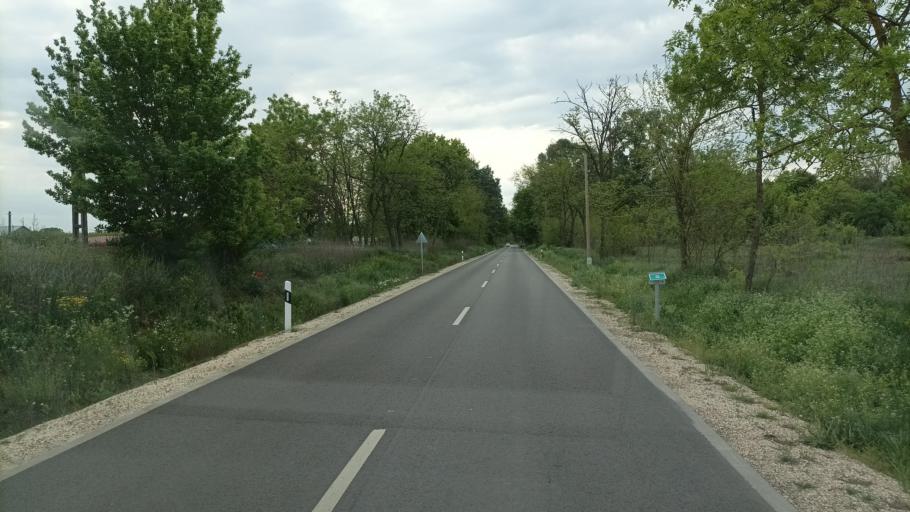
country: HU
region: Pest
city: Nyaregyhaza
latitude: 47.2892
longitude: 19.4524
